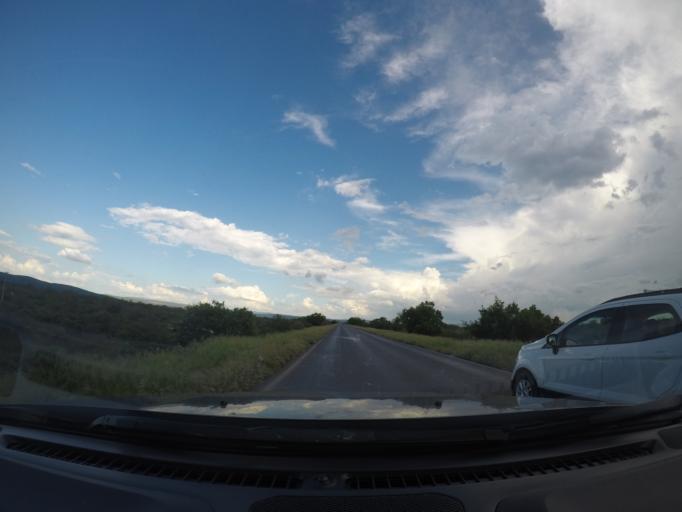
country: BR
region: Bahia
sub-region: Ibotirama
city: Ibotirama
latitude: -12.1578
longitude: -43.2987
